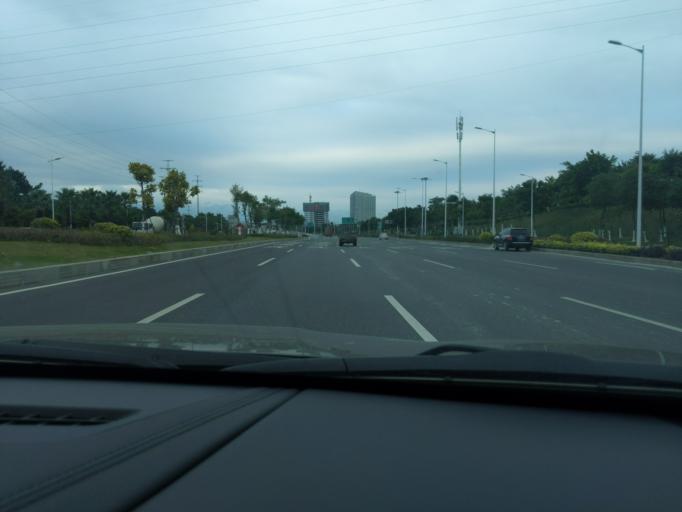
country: CN
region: Fujian
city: Maxiang
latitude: 24.6784
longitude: 118.2300
